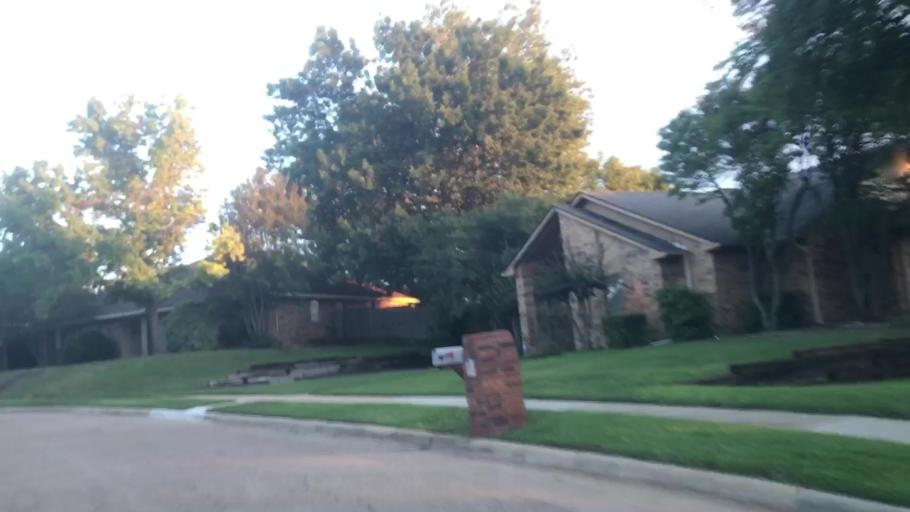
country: US
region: Texas
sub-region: Dallas County
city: Carrollton
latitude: 32.9744
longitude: -96.8820
